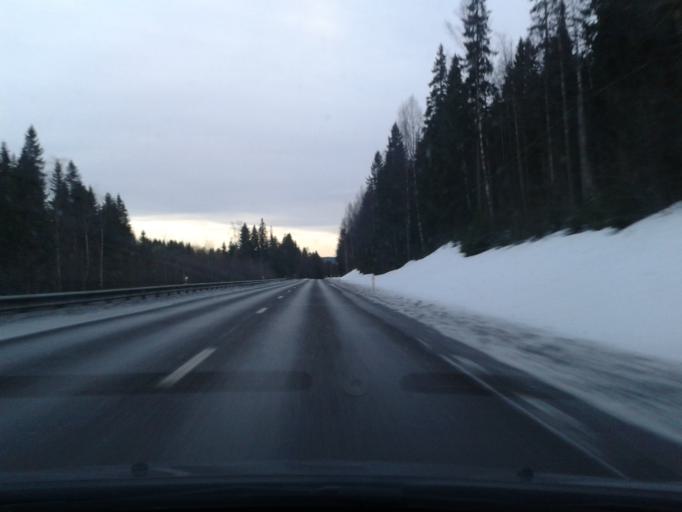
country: SE
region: Vaesternorrland
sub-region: Kramfors Kommun
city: Bollstabruk
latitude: 63.0958
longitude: 17.5244
